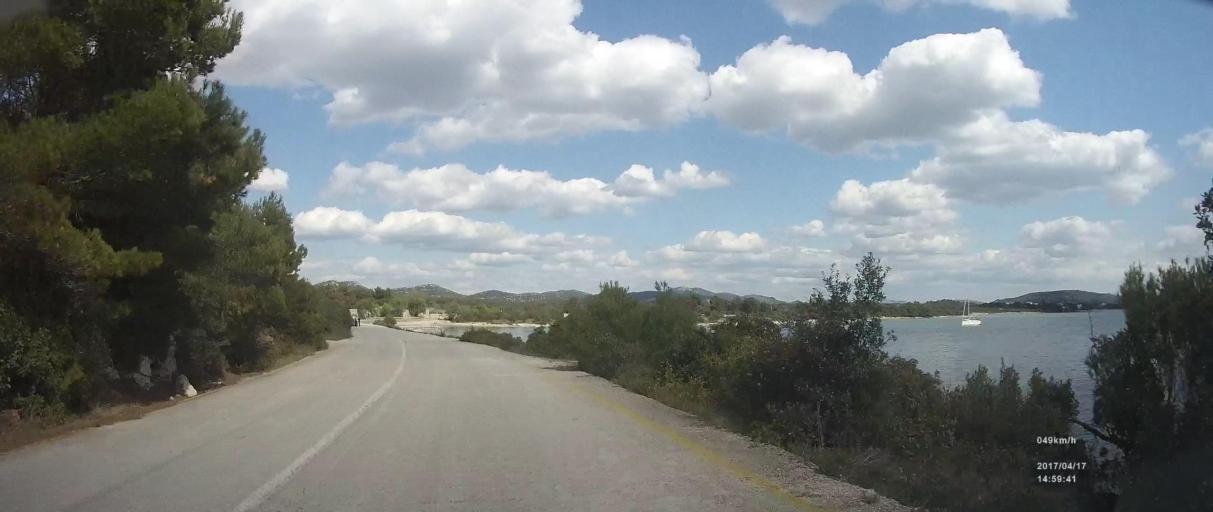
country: HR
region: Sibensko-Kniniska
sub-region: Grad Sibenik
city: Tisno
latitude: 43.8335
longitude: 15.6362
